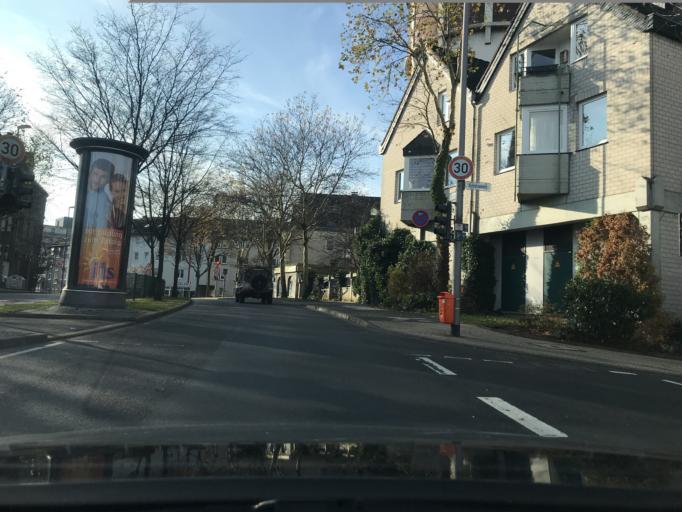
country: DE
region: North Rhine-Westphalia
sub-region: Regierungsbezirk Dusseldorf
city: Remscheid
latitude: 51.1832
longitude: 7.1850
